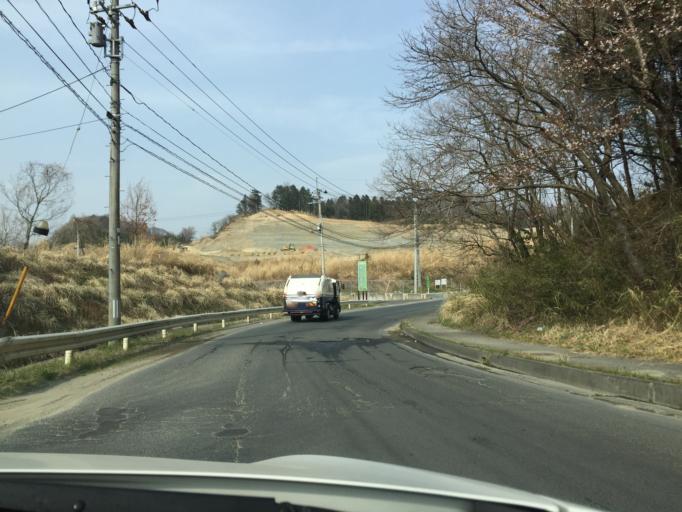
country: JP
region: Fukushima
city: Iwaki
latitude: 36.9681
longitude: 140.8500
